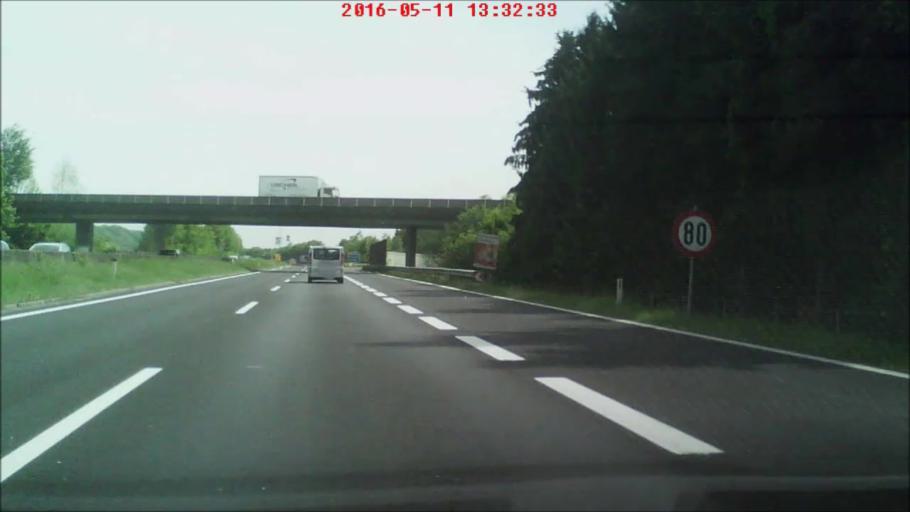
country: AT
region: Upper Austria
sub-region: Politischer Bezirk Scharding
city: Sankt Marienkirchen bei Schaerding
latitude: 48.3208
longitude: 13.4172
